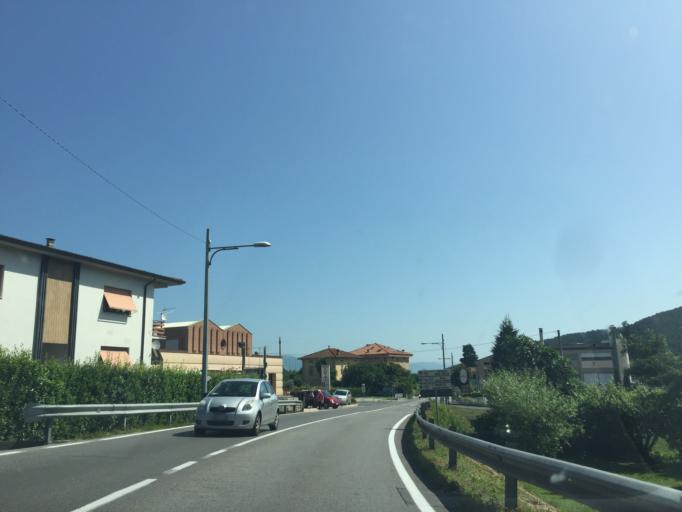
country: IT
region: Tuscany
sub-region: Province of Pisa
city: San Giuliano Terme
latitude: 43.7784
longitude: 10.4592
